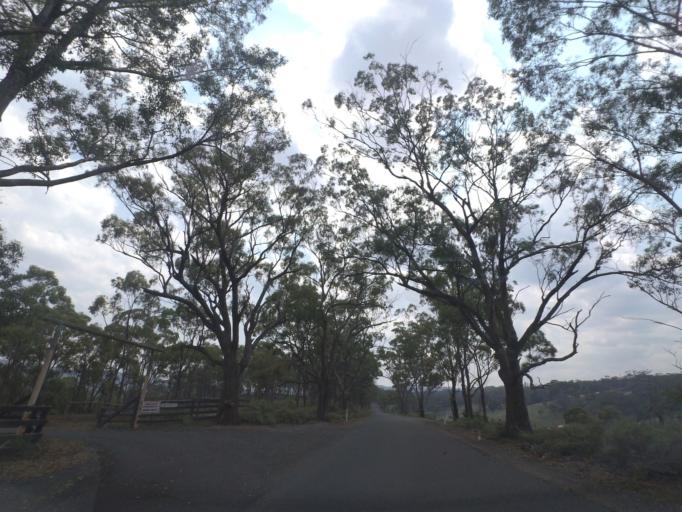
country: AU
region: Victoria
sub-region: Moorabool
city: Bacchus Marsh
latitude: -37.6143
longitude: 144.4394
